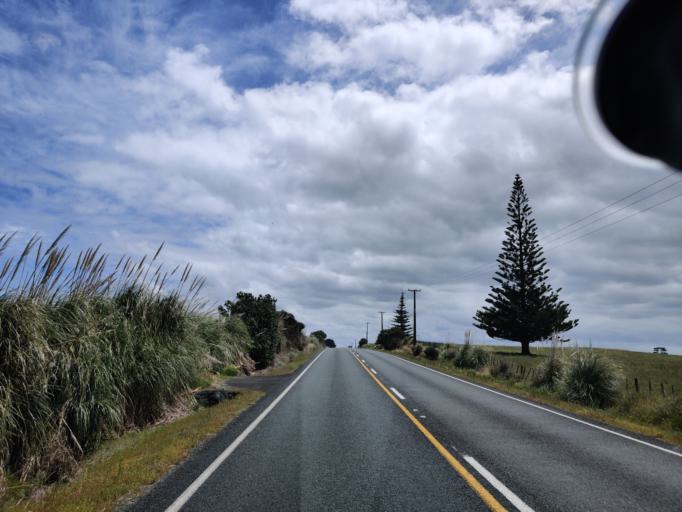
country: NZ
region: Northland
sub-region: Far North District
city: Kaitaia
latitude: -34.7005
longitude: 173.0280
